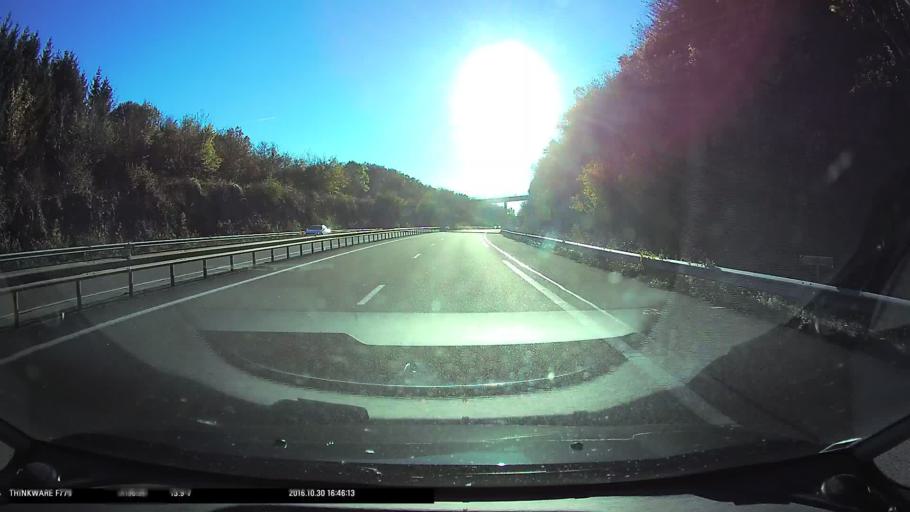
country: FR
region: Franche-Comte
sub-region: Departement du Doubs
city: Chatillon-le-Duc
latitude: 47.3006
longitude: 6.0321
